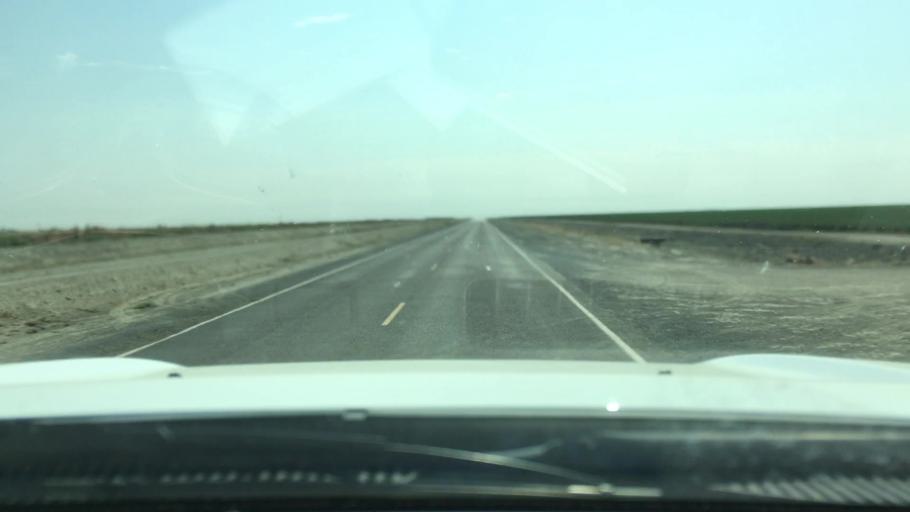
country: US
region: California
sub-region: Tulare County
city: Alpaugh
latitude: 35.9344
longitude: -119.6267
